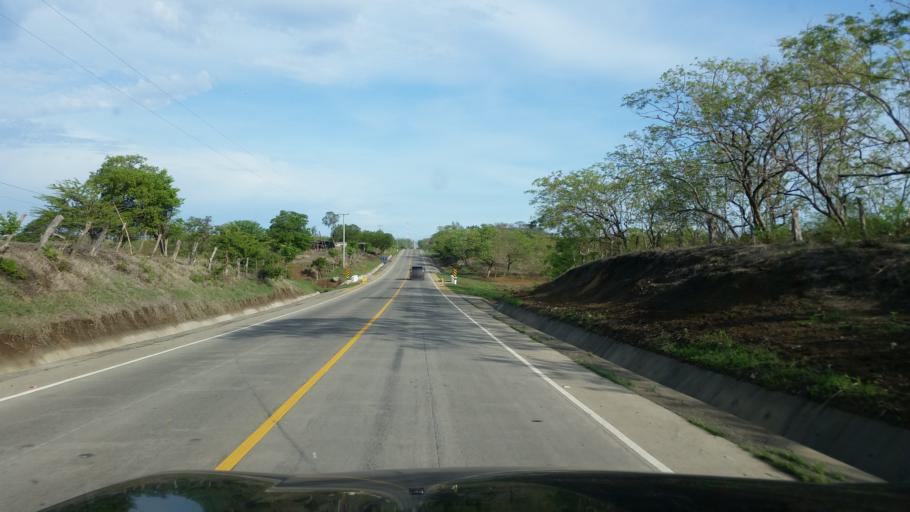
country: NI
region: Leon
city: Nagarote
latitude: 12.1116
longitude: -86.6014
